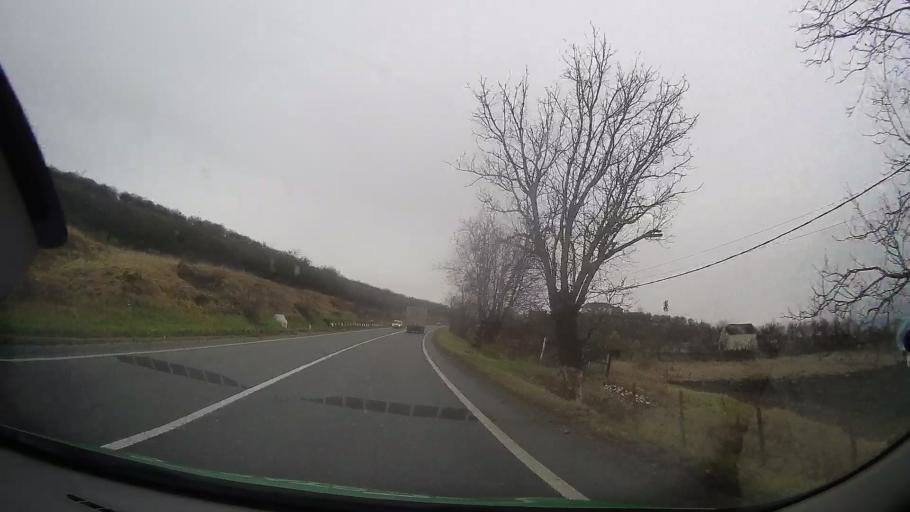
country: RO
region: Mures
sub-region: Comuna Breaza
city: Breaza
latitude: 46.7668
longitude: 24.6589
